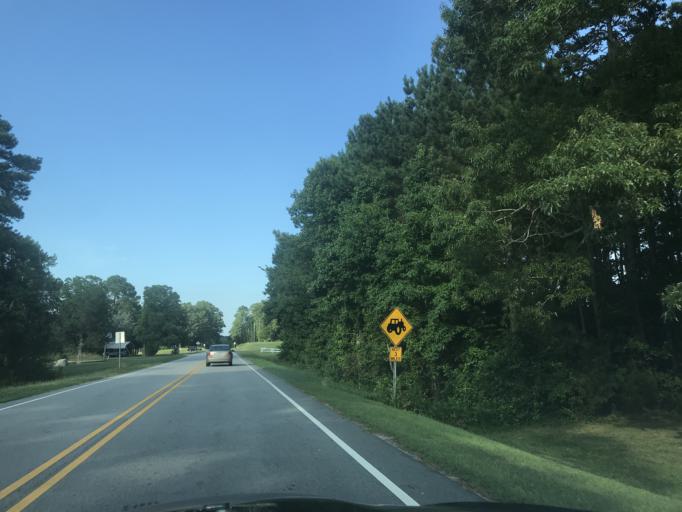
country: US
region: North Carolina
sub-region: Wake County
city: Rolesville
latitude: 35.9331
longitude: -78.4404
